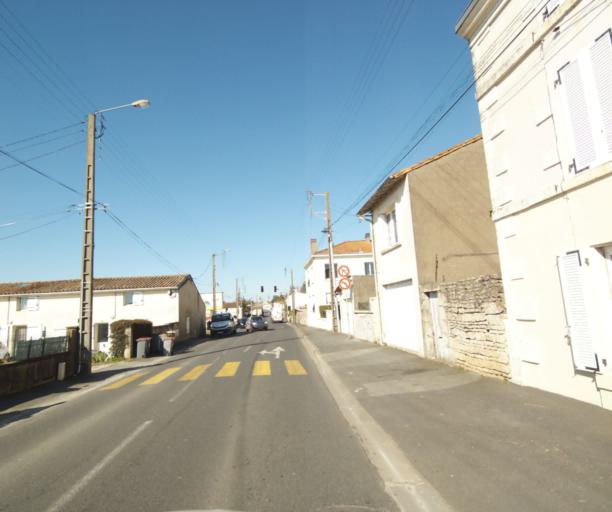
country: FR
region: Poitou-Charentes
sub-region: Departement des Deux-Sevres
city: Niort
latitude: 46.3473
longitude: -0.4772
